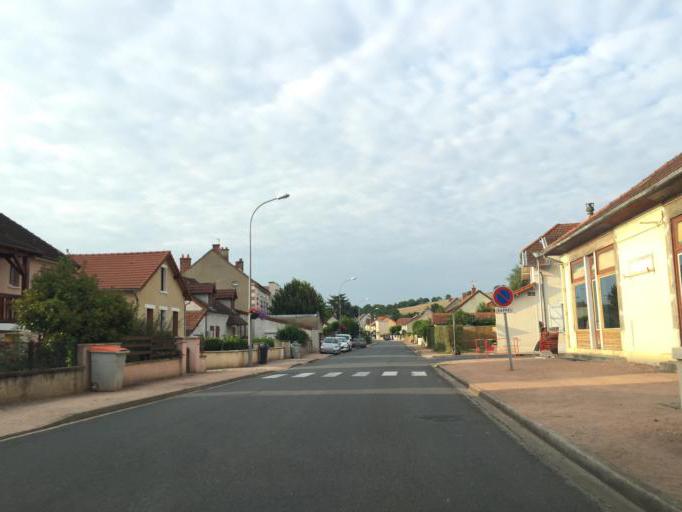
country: FR
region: Auvergne
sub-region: Departement de l'Allier
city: Saint-Germain-des-Fosses
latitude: 46.2134
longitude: 3.4322
